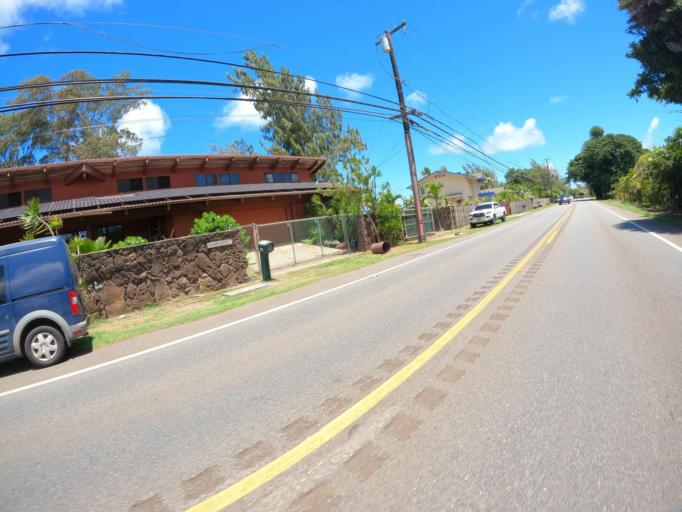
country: US
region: Hawaii
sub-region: Honolulu County
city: Pupukea
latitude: 21.6948
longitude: -158.0174
